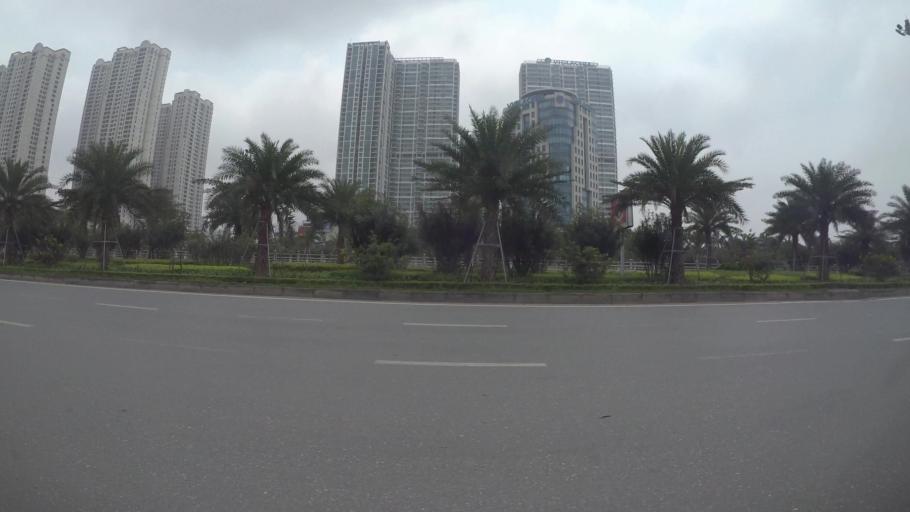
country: VN
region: Ha Noi
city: Thanh Xuan
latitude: 21.0046
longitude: 105.7908
